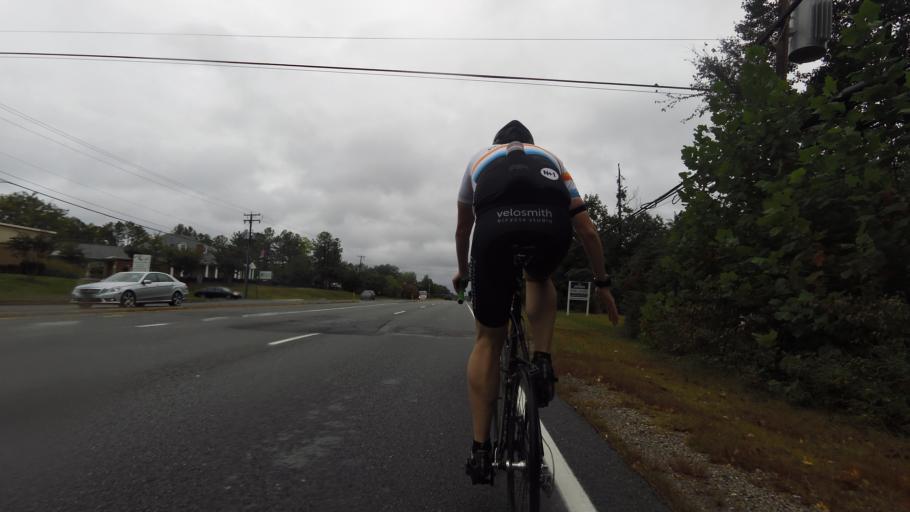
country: US
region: Virginia
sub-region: Henrico County
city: Tuckahoe
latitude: 37.5967
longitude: -77.6028
